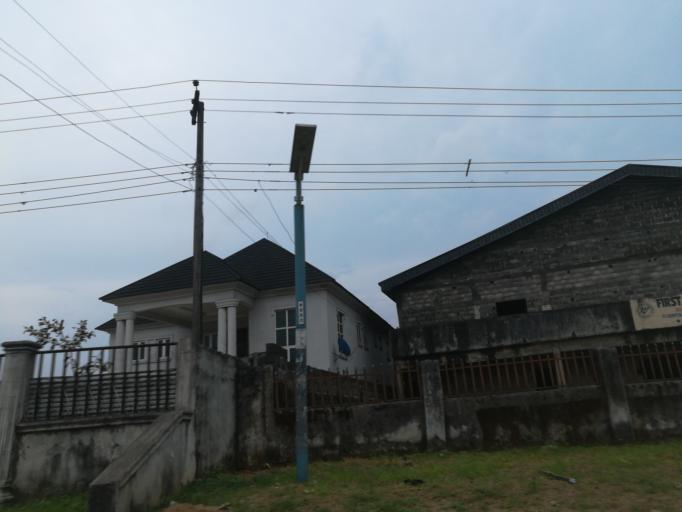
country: NG
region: Rivers
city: Okrika
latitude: 4.7849
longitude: 7.1268
